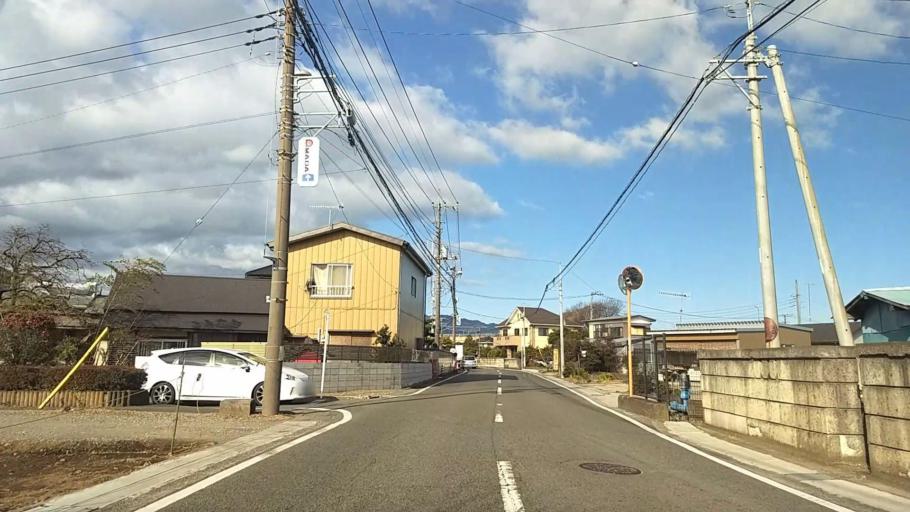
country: JP
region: Kanagawa
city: Atsugi
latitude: 35.4174
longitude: 139.3556
